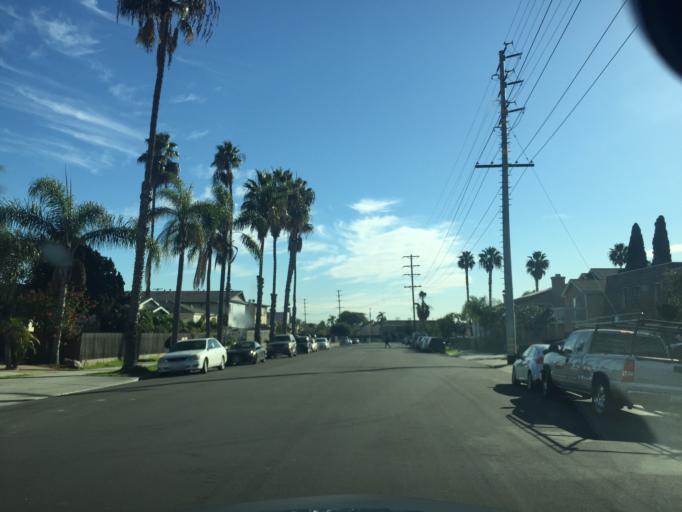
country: US
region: California
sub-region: San Diego County
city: San Diego
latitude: 32.7532
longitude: -117.1218
